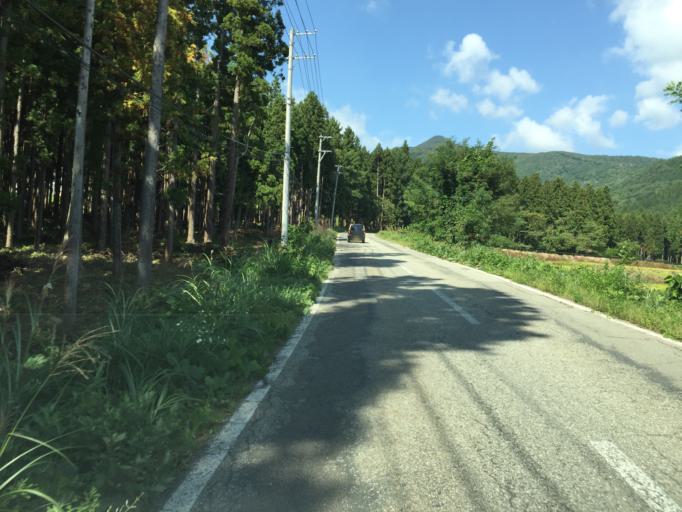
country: JP
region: Fukushima
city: Inawashiro
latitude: 37.5729
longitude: 140.0191
